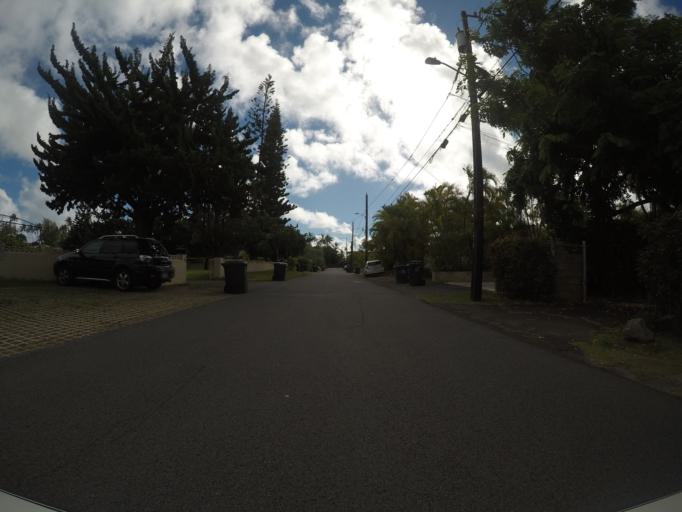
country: US
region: Hawaii
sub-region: Honolulu County
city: Kailua
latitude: 21.4022
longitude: -157.7409
